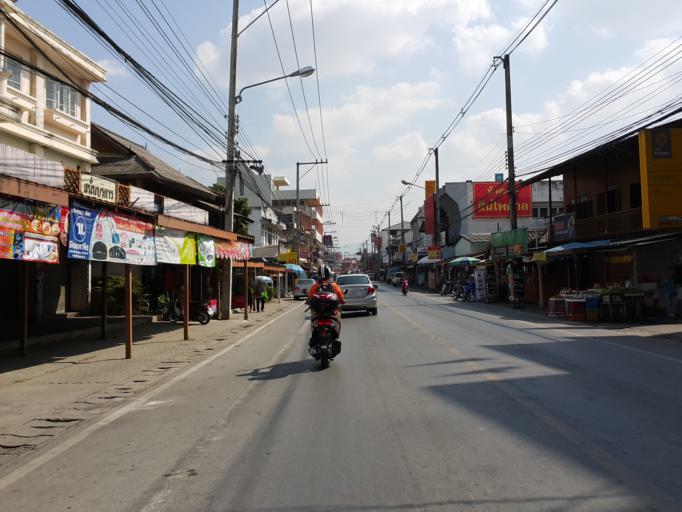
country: TH
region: Chiang Mai
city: San Kamphaeng
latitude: 18.7441
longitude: 99.1208
